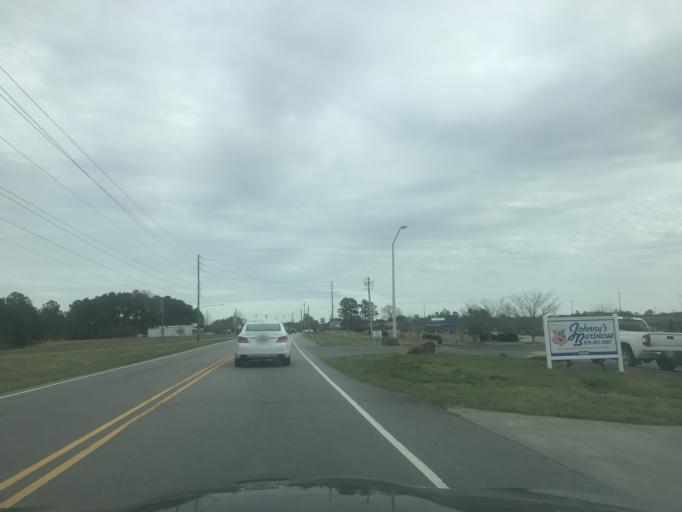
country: US
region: North Carolina
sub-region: Franklin County
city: Louisburg
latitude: 36.0860
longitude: -78.3204
